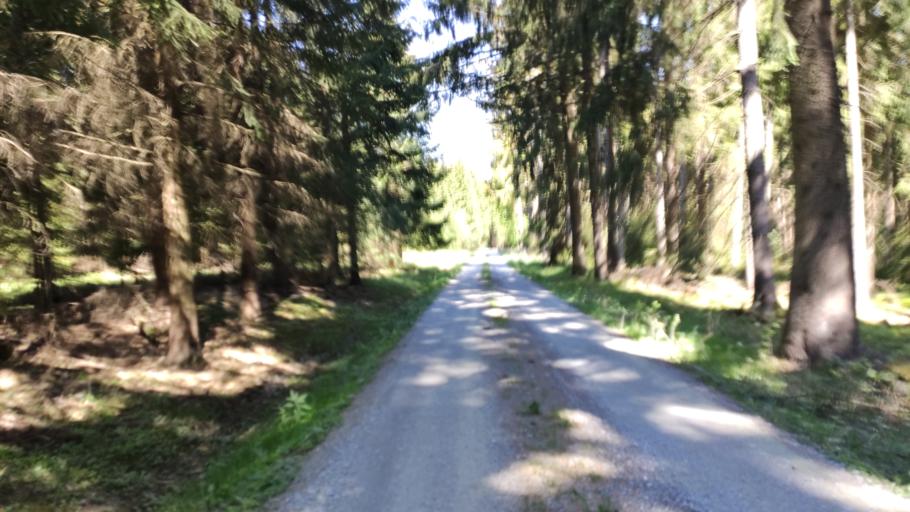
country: DE
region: Bavaria
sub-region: Upper Franconia
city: Reichenbach
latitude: 50.4562
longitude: 11.4310
